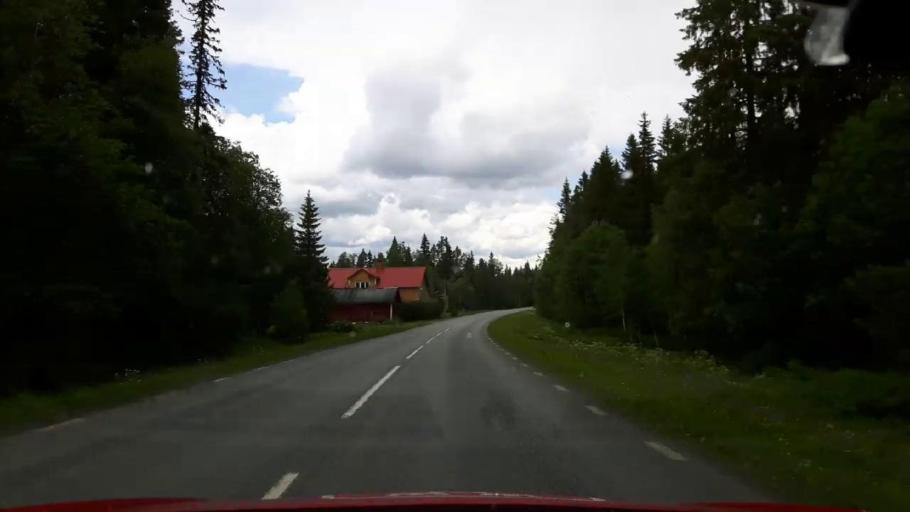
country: SE
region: Jaemtland
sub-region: Krokoms Kommun
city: Krokom
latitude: 63.5003
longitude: 14.2132
